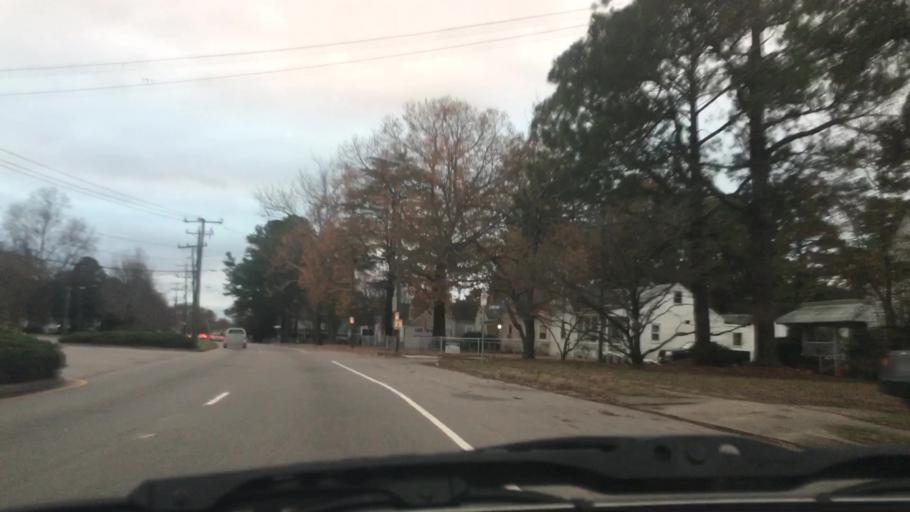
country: US
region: Virginia
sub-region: City of Norfolk
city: Norfolk
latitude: 36.8833
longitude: -76.2465
